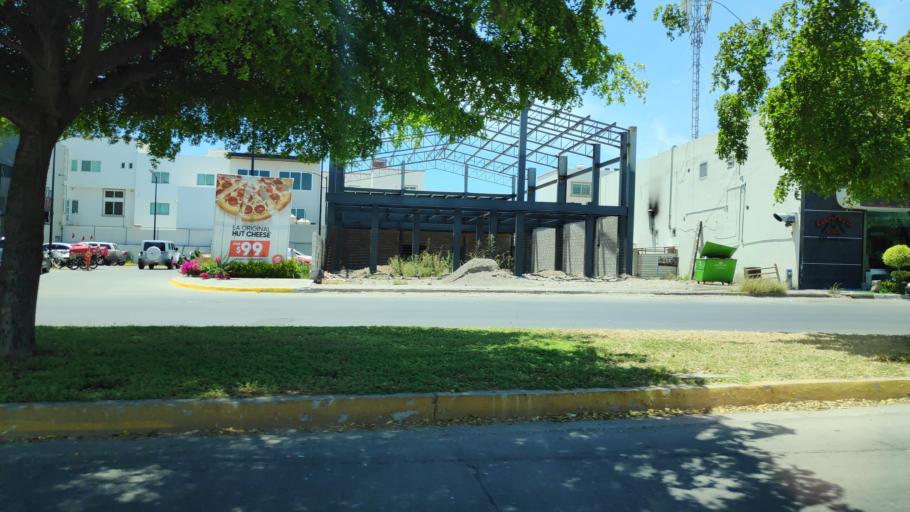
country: MX
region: Sinaloa
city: Culiacan
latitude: 24.8271
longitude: -107.3998
